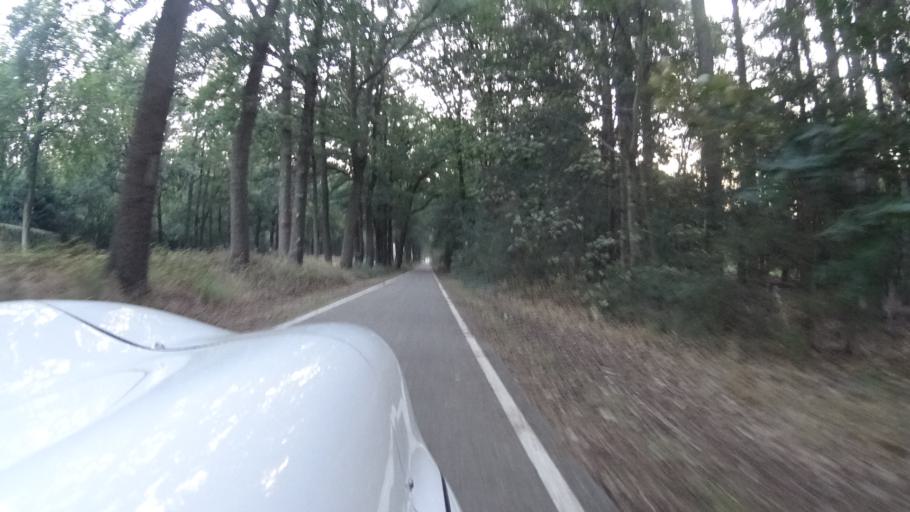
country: NL
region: North Brabant
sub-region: Gemeente Mill en Sint Hubert
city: Wilbertoord
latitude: 51.5881
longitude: 5.8072
